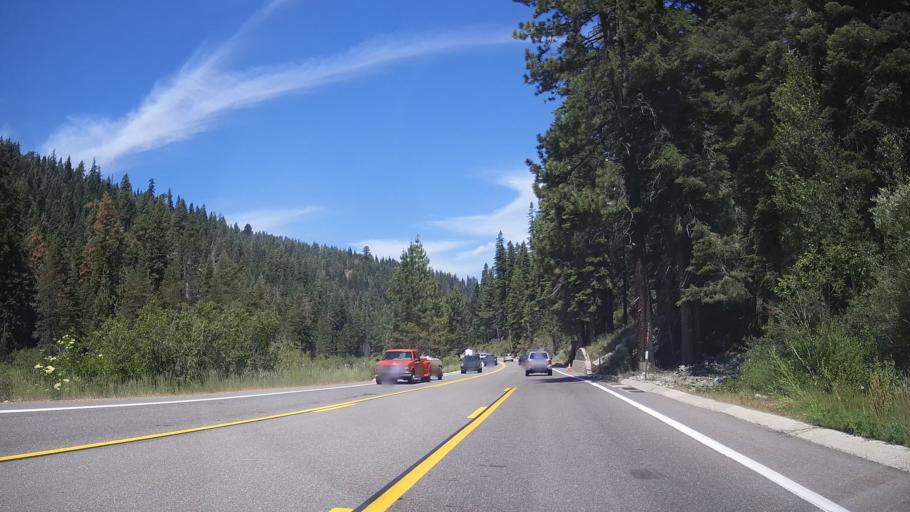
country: US
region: California
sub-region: Placer County
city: Sunnyside-Tahoe City
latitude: 39.1681
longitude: -120.1834
